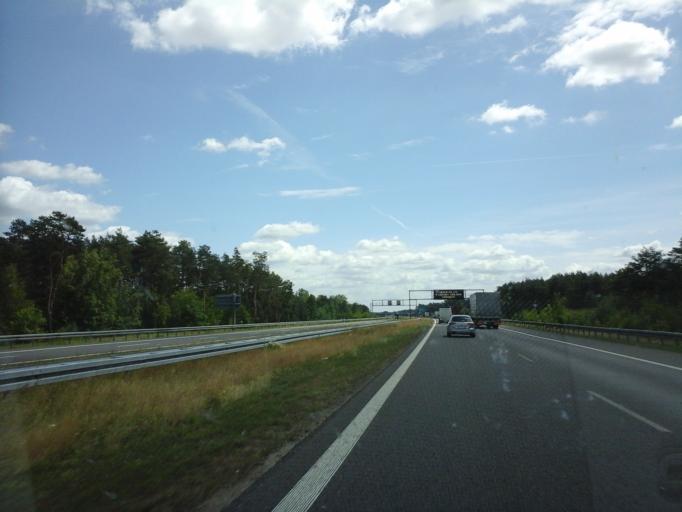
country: PL
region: Greater Poland Voivodeship
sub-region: Powiat kolski
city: Dabie
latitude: 52.0820
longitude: 18.7966
